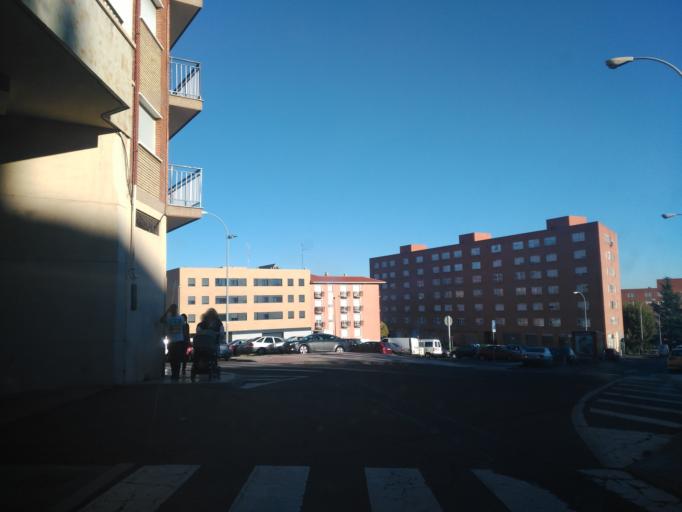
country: ES
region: Castille and Leon
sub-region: Provincia de Salamanca
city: Salamanca
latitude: 40.9683
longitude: -5.6466
